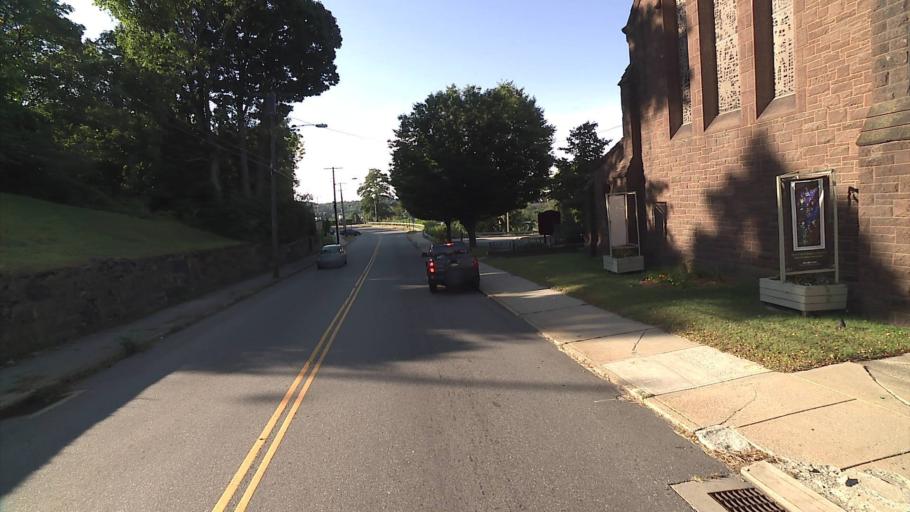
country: US
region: Connecticut
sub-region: New London County
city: Norwich
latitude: 41.5269
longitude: -72.0823
